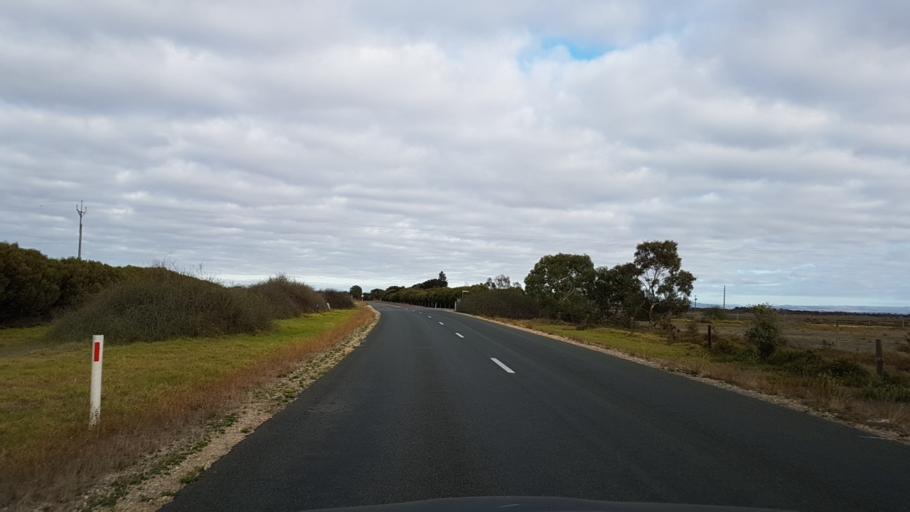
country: AU
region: South Australia
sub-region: Alexandrina
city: Langhorne Creek
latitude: -35.3946
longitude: 139.0051
